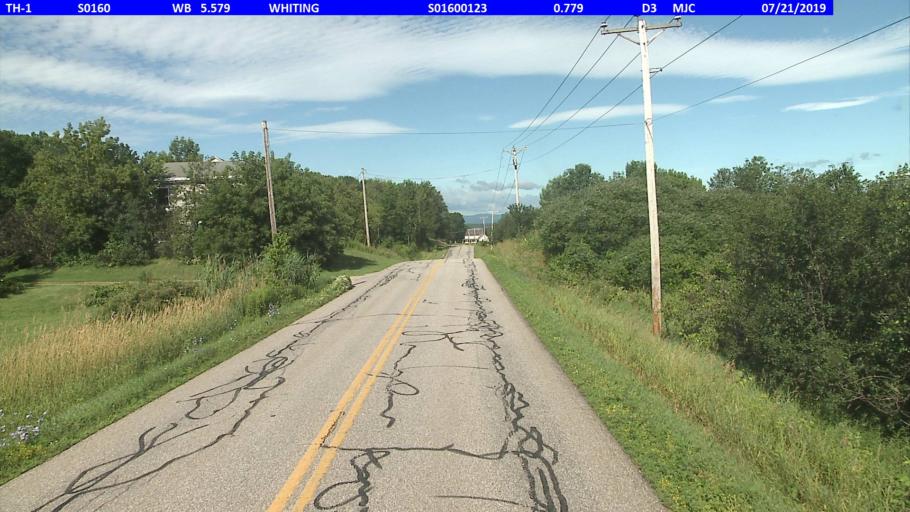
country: US
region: Vermont
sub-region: Rutland County
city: Brandon
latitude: 43.8633
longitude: -73.2103
